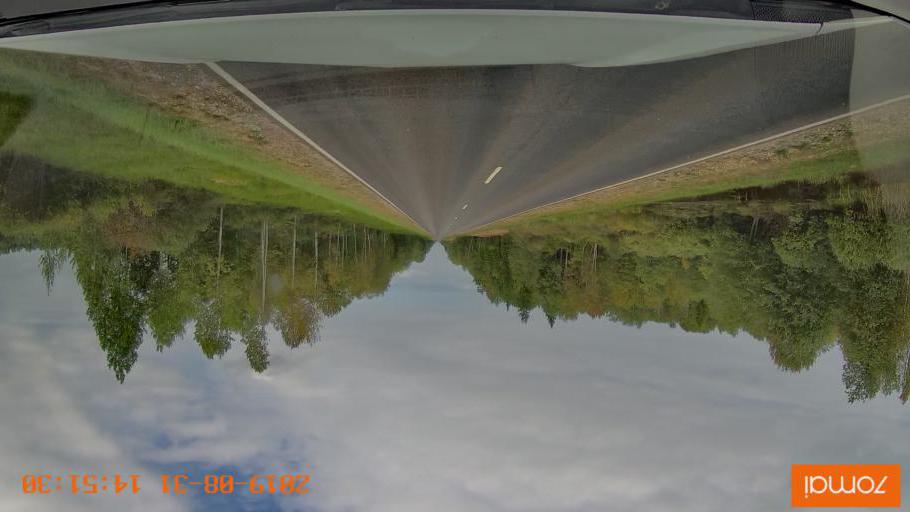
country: RU
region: Kaluga
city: Spas-Demensk
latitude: 54.2691
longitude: 33.8160
